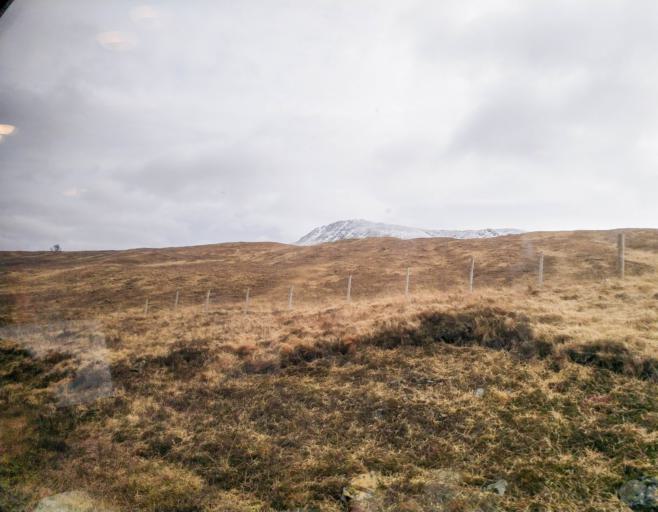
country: GB
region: Scotland
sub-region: Highland
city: Spean Bridge
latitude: 56.5452
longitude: -4.7550
